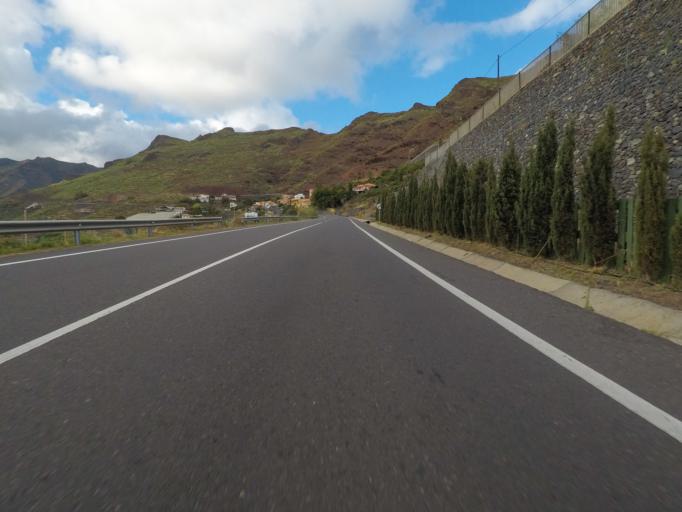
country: ES
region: Canary Islands
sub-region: Provincia de Santa Cruz de Tenerife
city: San Sebastian de la Gomera
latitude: 28.1069
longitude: -17.1253
